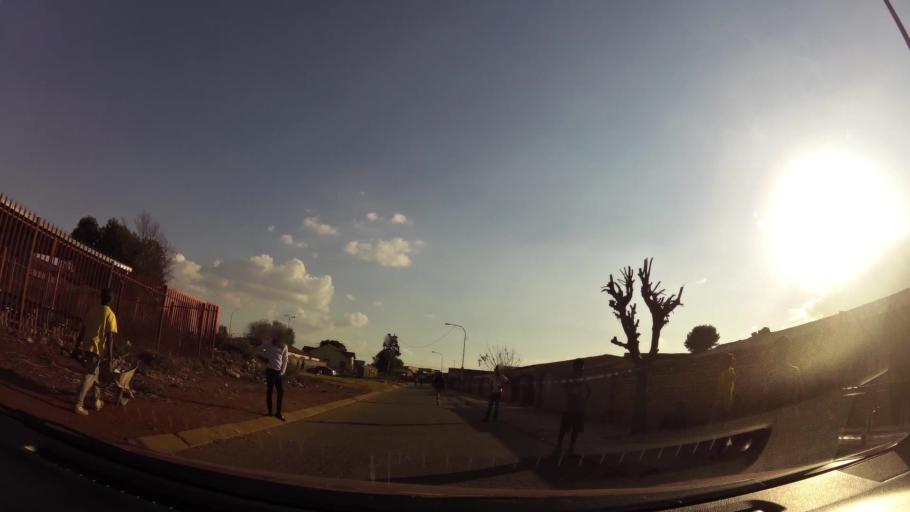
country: ZA
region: Gauteng
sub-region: City of Johannesburg Metropolitan Municipality
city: Soweto
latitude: -26.2270
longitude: 27.8603
